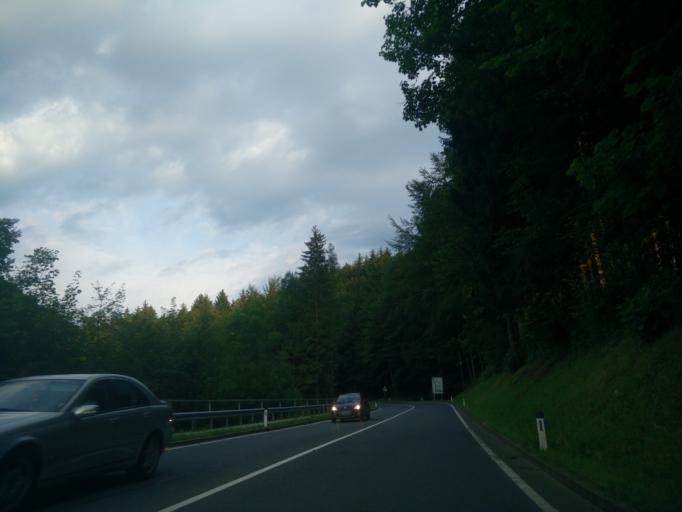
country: AT
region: Salzburg
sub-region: Politischer Bezirk Salzburg-Umgebung
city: Plainfeld
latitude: 47.8142
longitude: 13.1774
